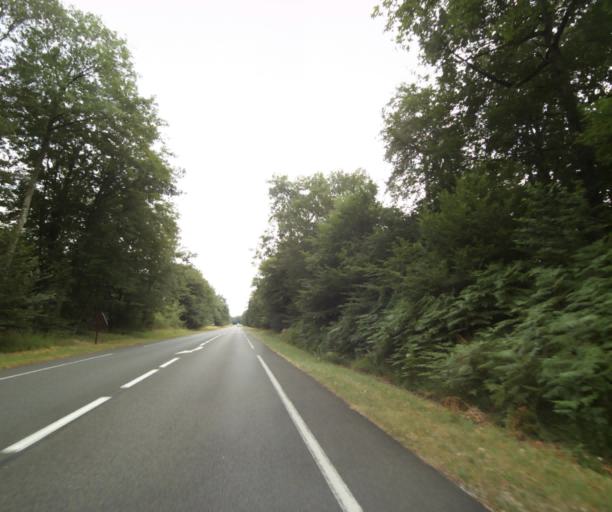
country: FR
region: Ile-de-France
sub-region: Departement de Seine-et-Marne
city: Bois-le-Roi
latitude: 48.4592
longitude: 2.6833
